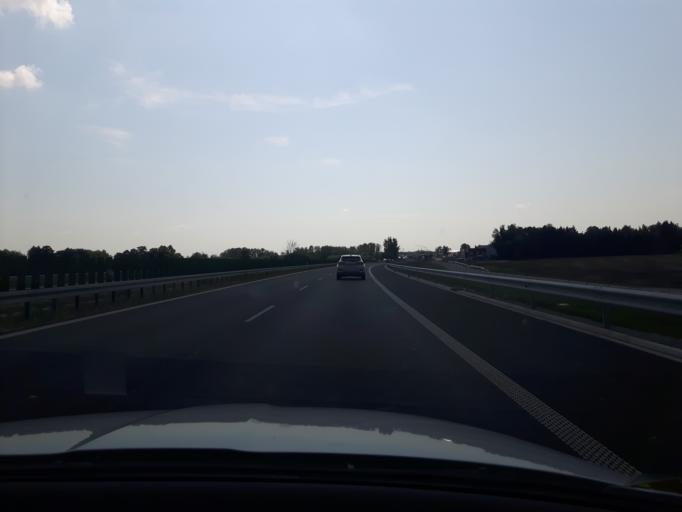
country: PL
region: Warmian-Masurian Voivodeship
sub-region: Powiat elblaski
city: Elblag
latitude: 54.1573
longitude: 19.3624
